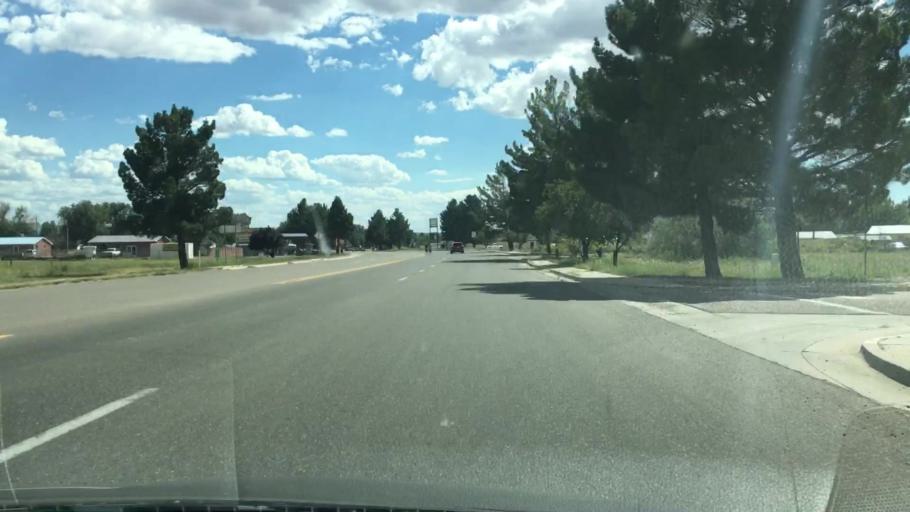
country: US
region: Arizona
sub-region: Coconino County
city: Fredonia
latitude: 36.9576
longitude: -112.5271
